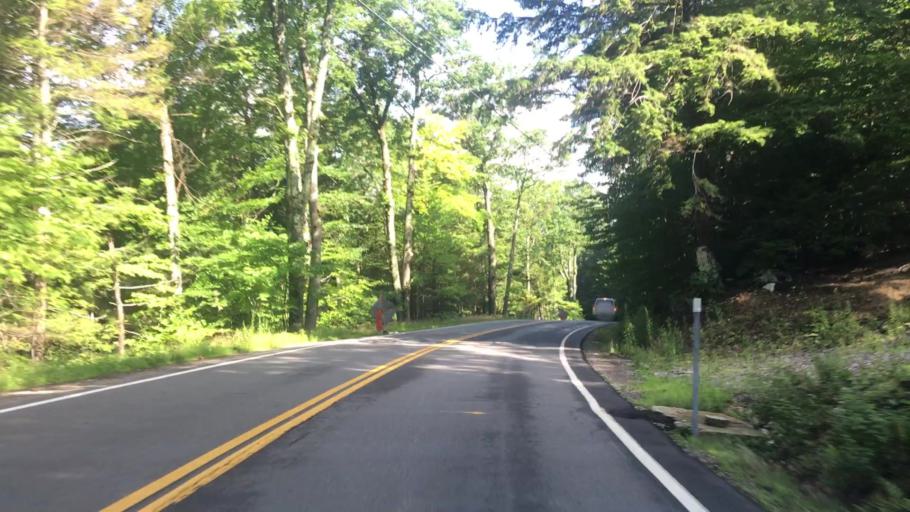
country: US
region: New Hampshire
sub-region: Belknap County
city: Gilford
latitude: 43.5431
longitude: -71.3499
